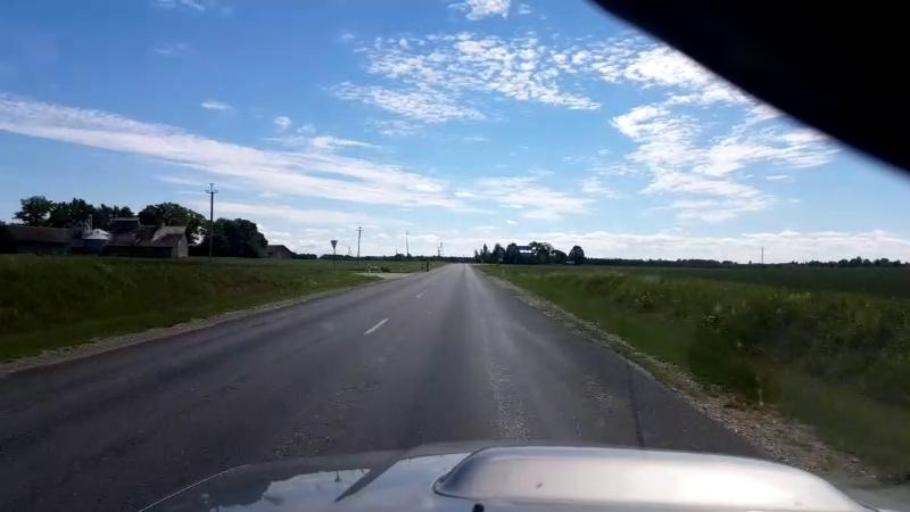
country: EE
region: Laeaene-Virumaa
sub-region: Rakke vald
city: Rakke
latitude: 58.9009
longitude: 26.2825
